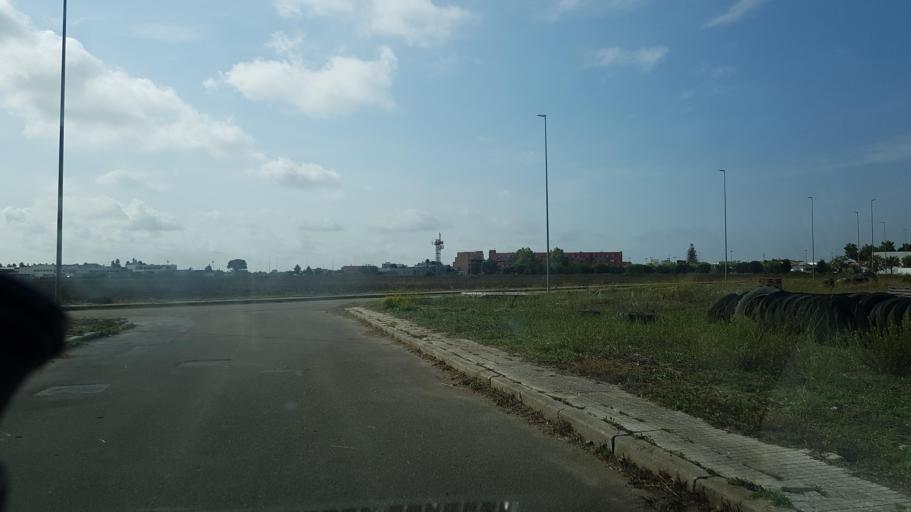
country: IT
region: Apulia
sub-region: Provincia di Brindisi
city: San Donaci
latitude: 40.4473
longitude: 17.9313
